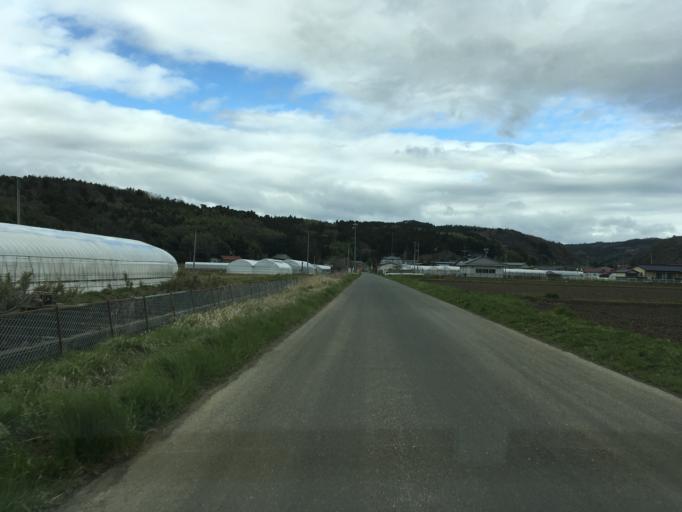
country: JP
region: Iwate
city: Ichinoseki
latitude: 38.7588
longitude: 141.2664
